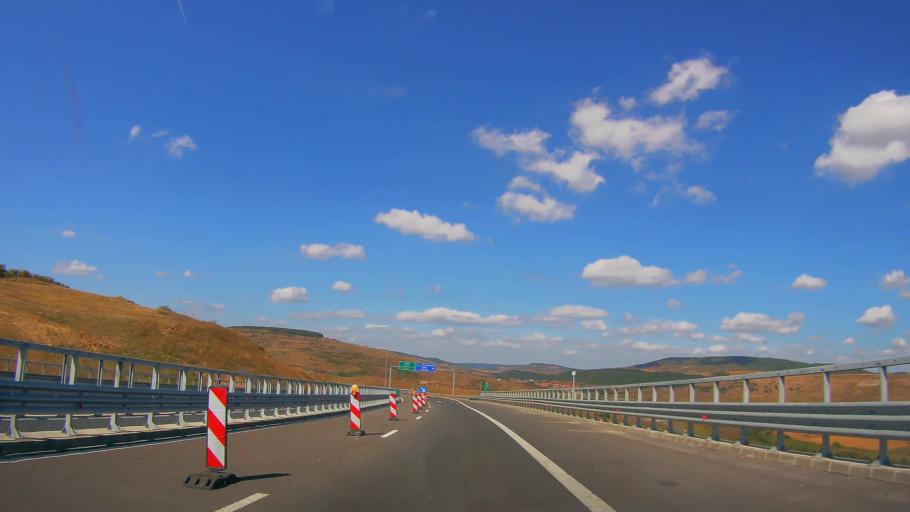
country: RO
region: Cluj
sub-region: Comuna Baciu
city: Mera
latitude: 46.8031
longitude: 23.4272
